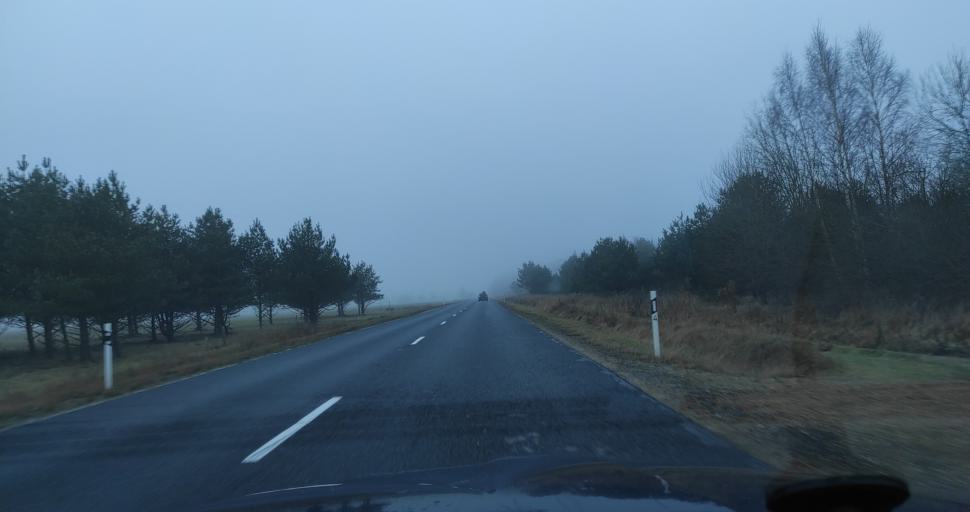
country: LV
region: Alsunga
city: Alsunga
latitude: 57.1116
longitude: 21.4228
